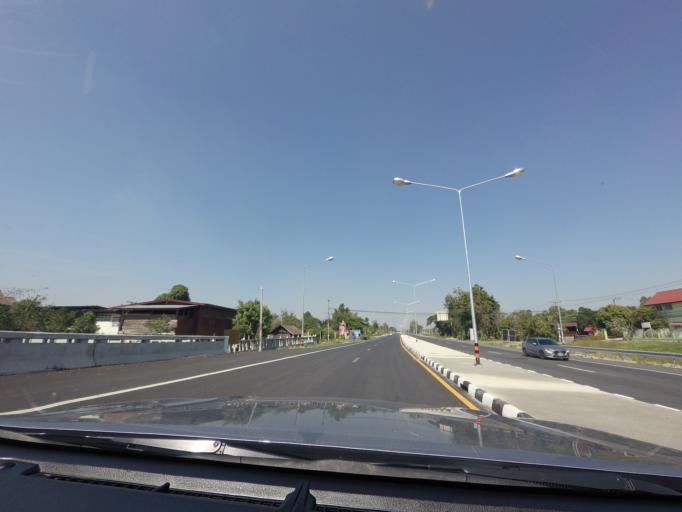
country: TH
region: Sukhothai
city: Ban Na
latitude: 17.0179
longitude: 99.7338
